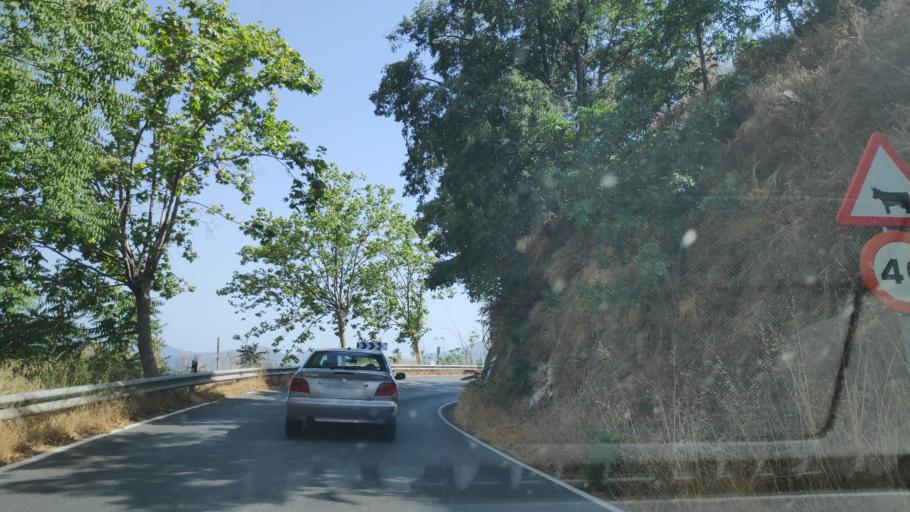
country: ES
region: Andalusia
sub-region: Provincia de Granada
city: Pampaneira
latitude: 36.9227
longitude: -3.3793
